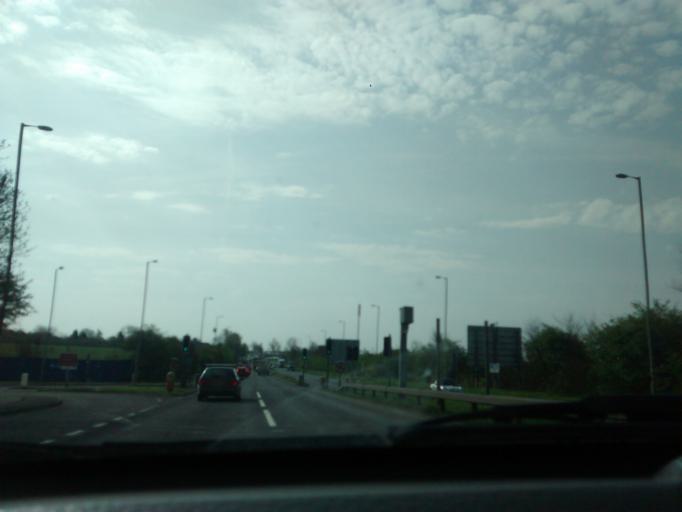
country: GB
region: England
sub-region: Oxfordshire
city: Yarnton
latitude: 51.7933
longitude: -1.2843
